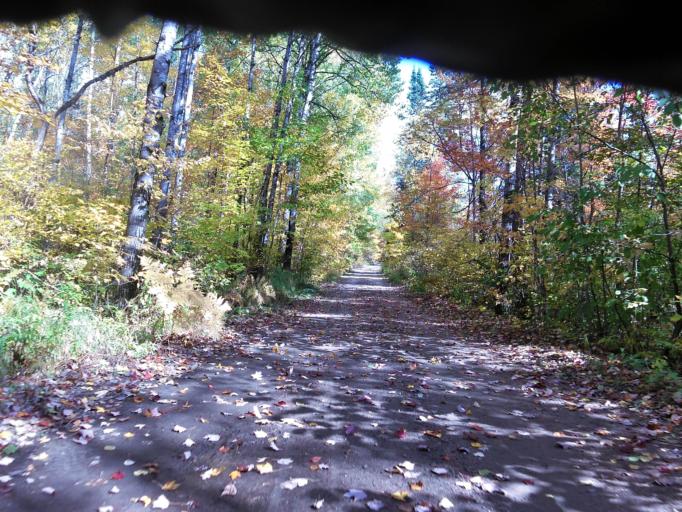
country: CA
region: Ontario
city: Petawawa
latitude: 45.8033
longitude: -77.2991
